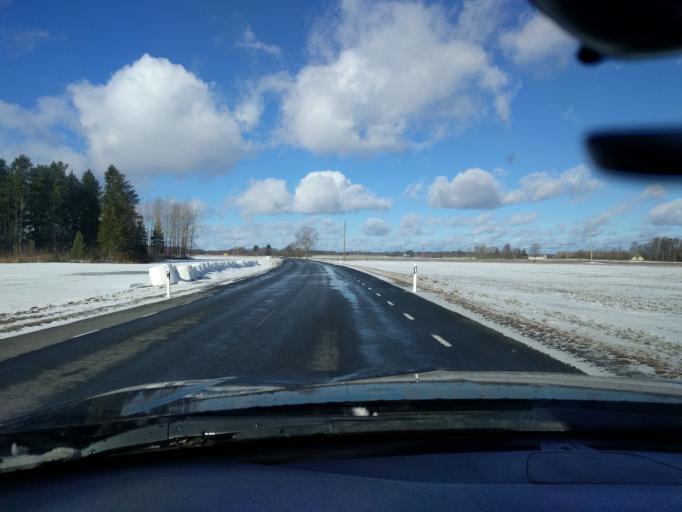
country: EE
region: Harju
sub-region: Anija vald
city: Kehra
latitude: 59.2472
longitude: 25.3501
